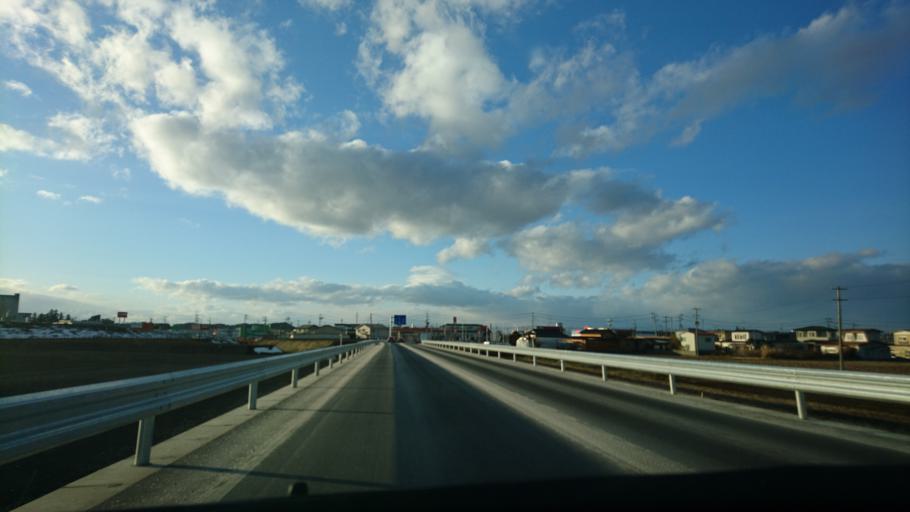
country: JP
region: Miyagi
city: Wakuya
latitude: 38.6955
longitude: 141.2150
